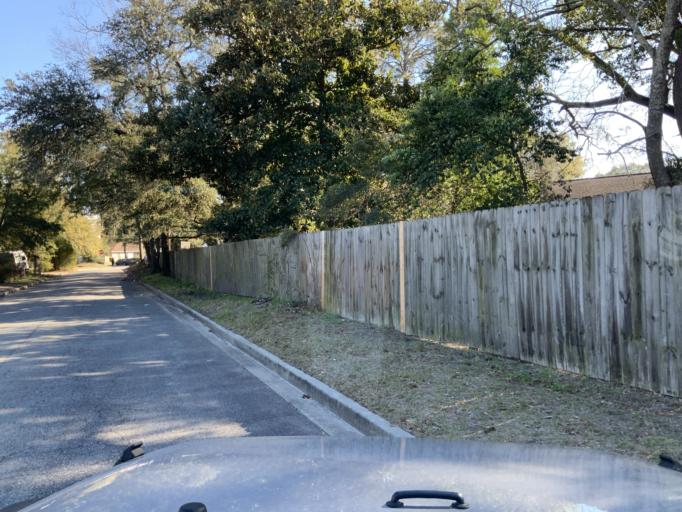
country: US
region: Georgia
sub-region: Chatham County
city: Thunderbolt
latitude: 32.0553
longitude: -81.0620
